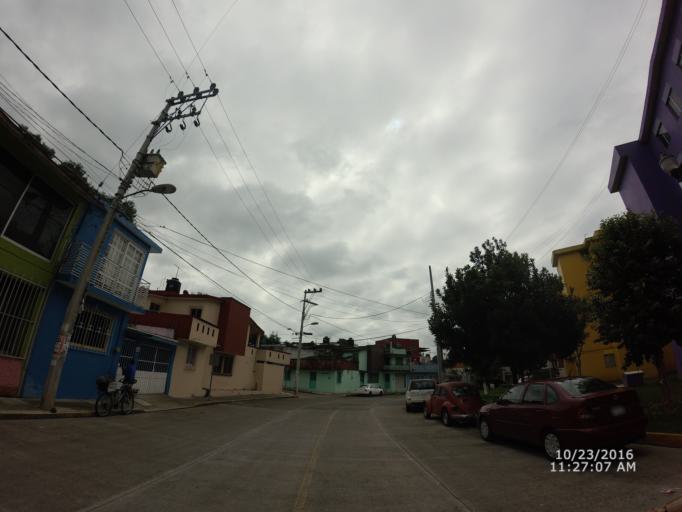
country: MX
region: Veracruz
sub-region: Tlalnelhuayocan
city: Guadalupe Victoria
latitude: 19.5488
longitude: -96.9404
